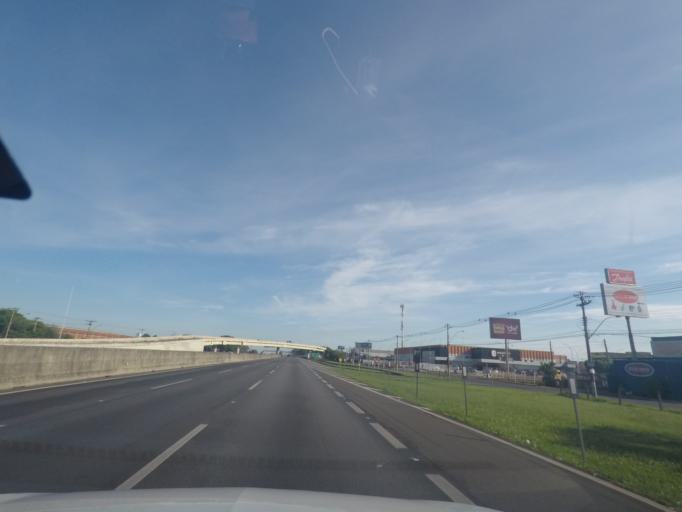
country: BR
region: Sao Paulo
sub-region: Americana
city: Americana
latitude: -22.7184
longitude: -47.2949
